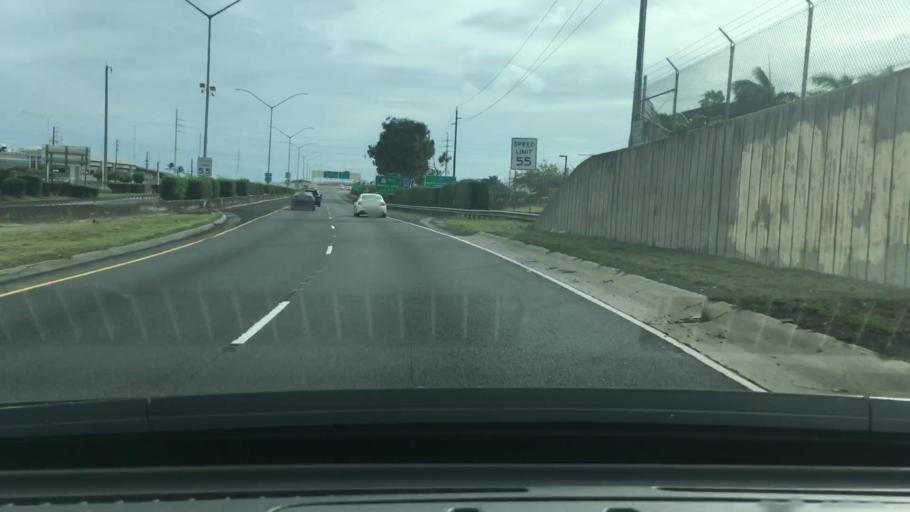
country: US
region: Hawaii
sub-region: Honolulu County
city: Honolulu
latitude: 21.3375
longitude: -157.8852
